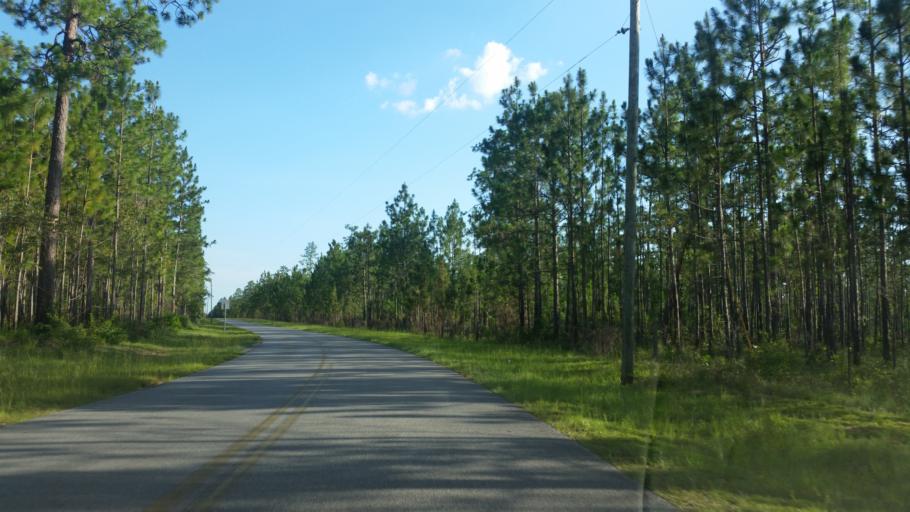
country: US
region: Florida
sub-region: Santa Rosa County
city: East Milton
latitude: 30.6917
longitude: -86.8760
